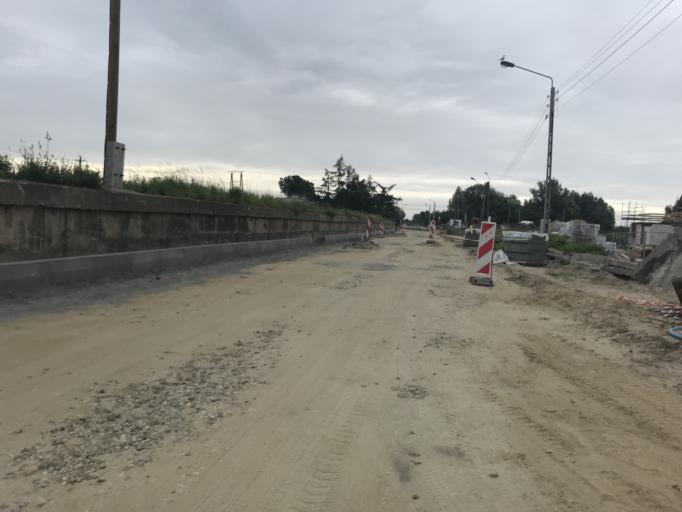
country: PL
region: Pomeranian Voivodeship
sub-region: Gdansk
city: Gdansk
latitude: 54.3416
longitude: 18.6846
